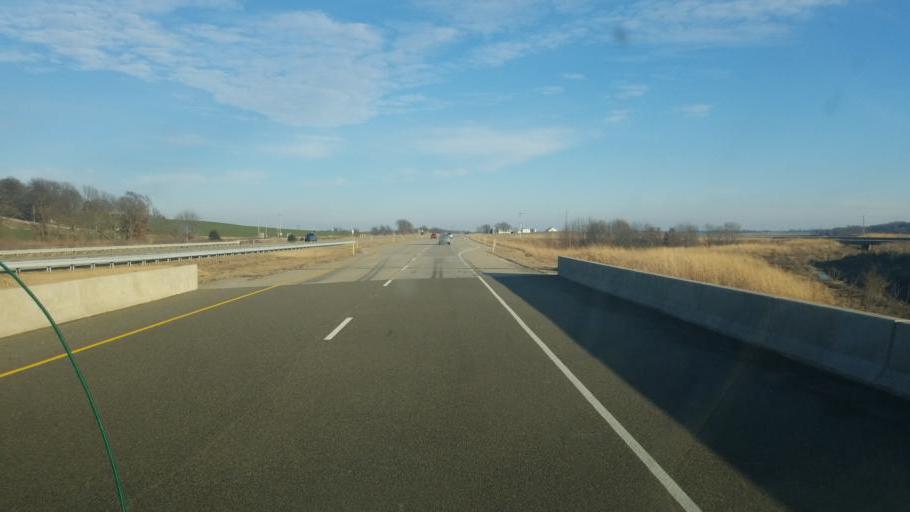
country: US
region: Indiana
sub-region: Knox County
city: Bicknell
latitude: 38.6755
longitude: -87.3720
